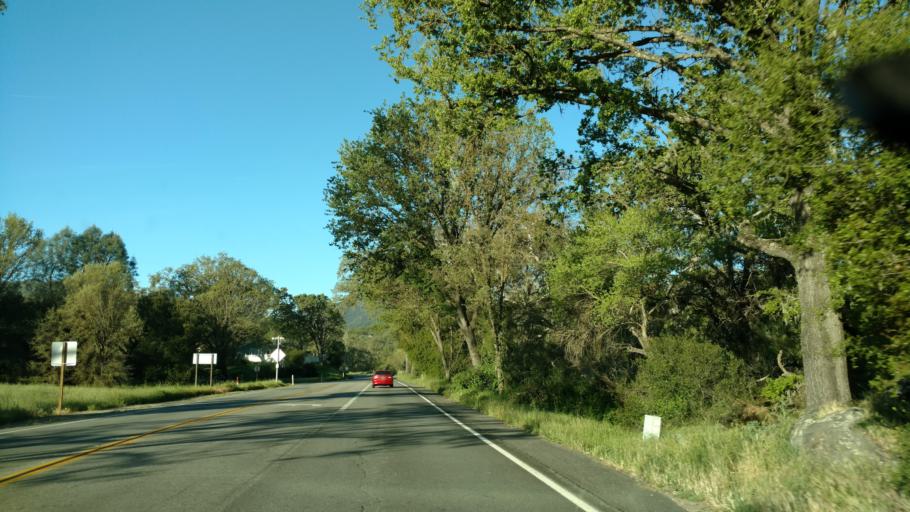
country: US
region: California
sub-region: San Luis Obispo County
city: Atascadero
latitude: 35.4624
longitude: -120.6758
